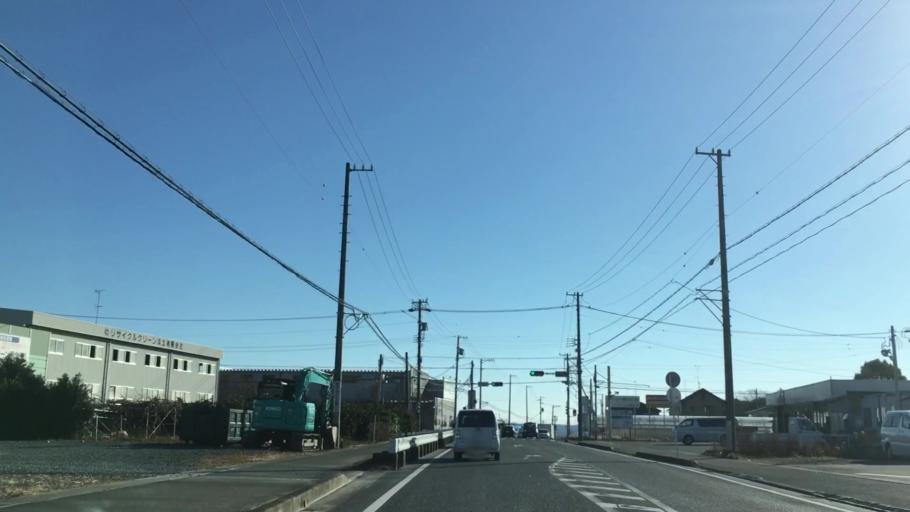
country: JP
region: Shizuoka
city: Hamakita
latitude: 34.8003
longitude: 137.7494
